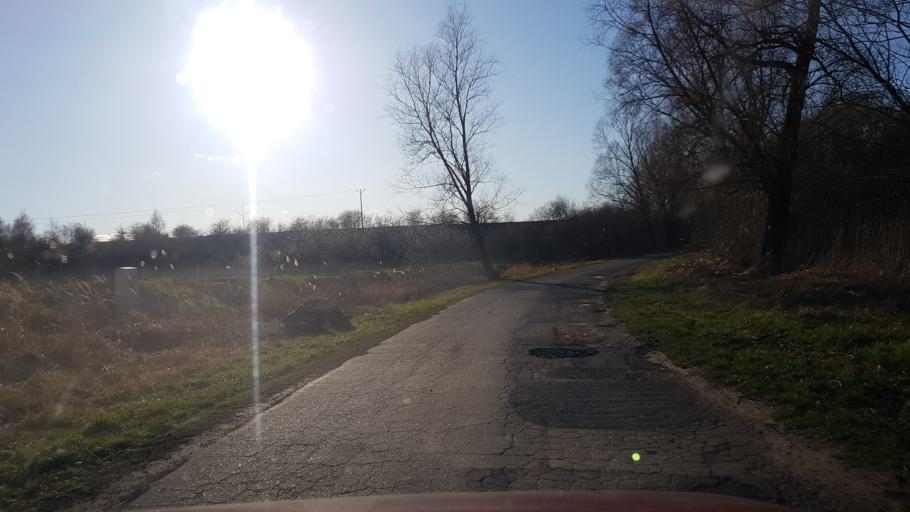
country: PL
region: West Pomeranian Voivodeship
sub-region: Powiat stargardzki
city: Stara Dabrowa
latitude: 53.3822
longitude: 15.0964
